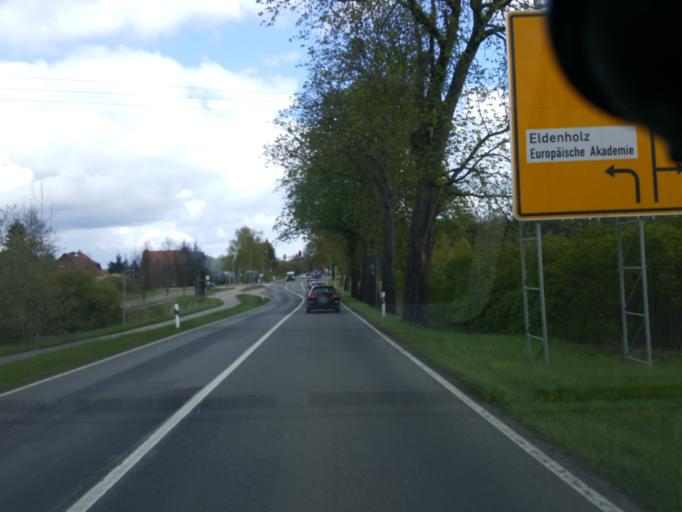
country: DE
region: Mecklenburg-Vorpommern
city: Waren
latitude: 53.5121
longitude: 12.6413
